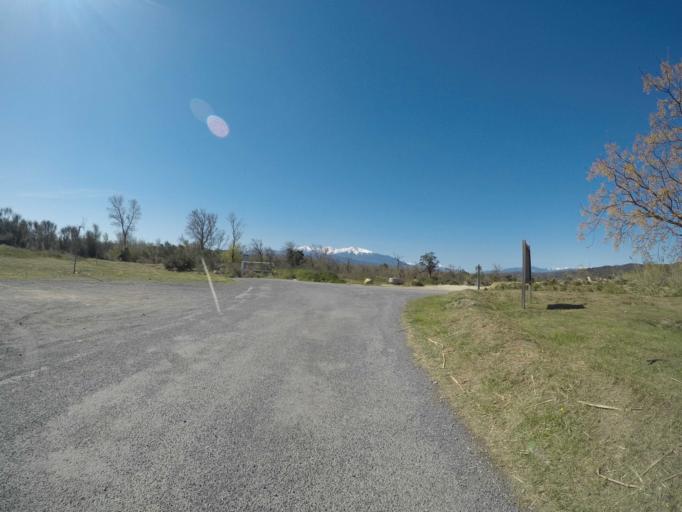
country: FR
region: Languedoc-Roussillon
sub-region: Departement des Pyrenees-Orientales
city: Millas
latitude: 42.6977
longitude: 2.6641
